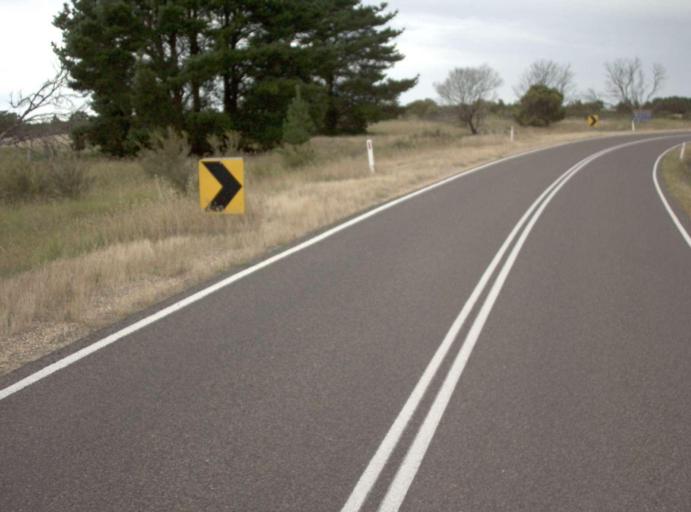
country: AU
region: Victoria
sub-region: East Gippsland
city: Bairnsdale
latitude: -37.9987
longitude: 147.3984
